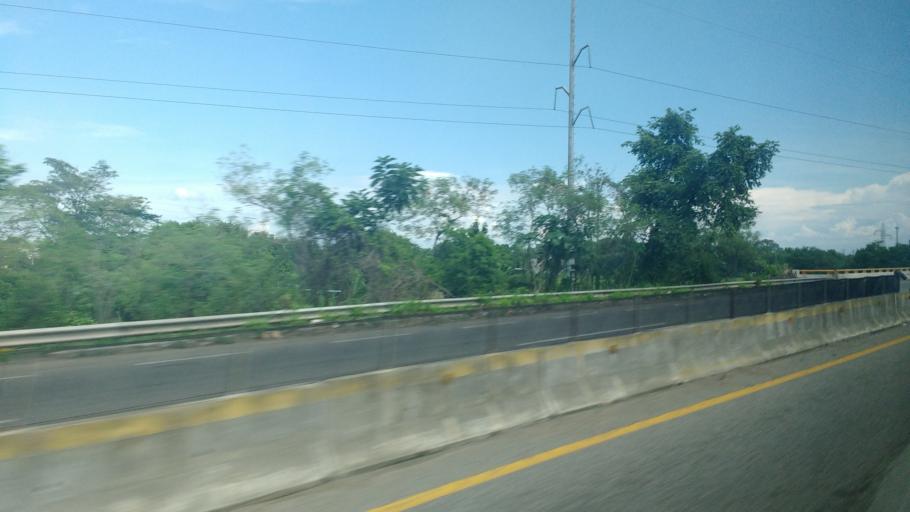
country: MX
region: Tabasco
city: Parrilla
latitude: 17.9141
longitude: -92.9233
